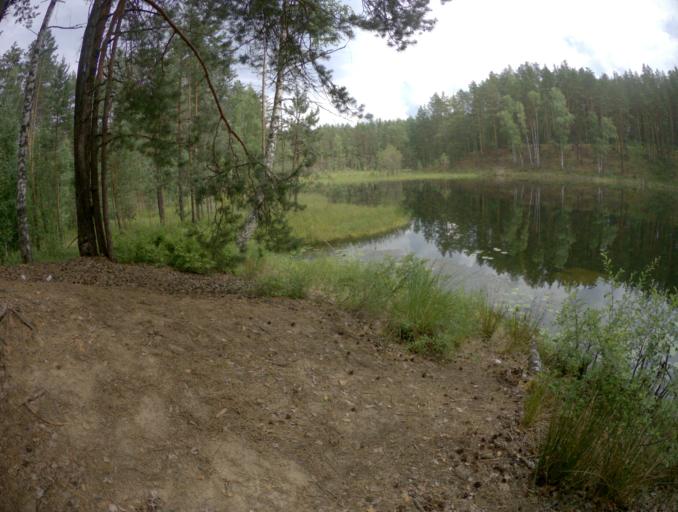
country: RU
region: Nizjnij Novgorod
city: Frolishchi
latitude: 56.3522
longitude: 42.7579
